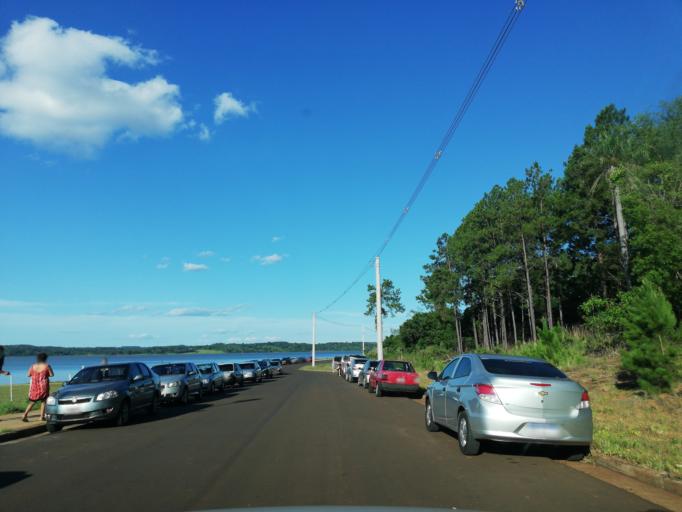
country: AR
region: Misiones
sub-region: Departamento de Candelaria
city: Candelaria
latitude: -27.4517
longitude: -55.7811
